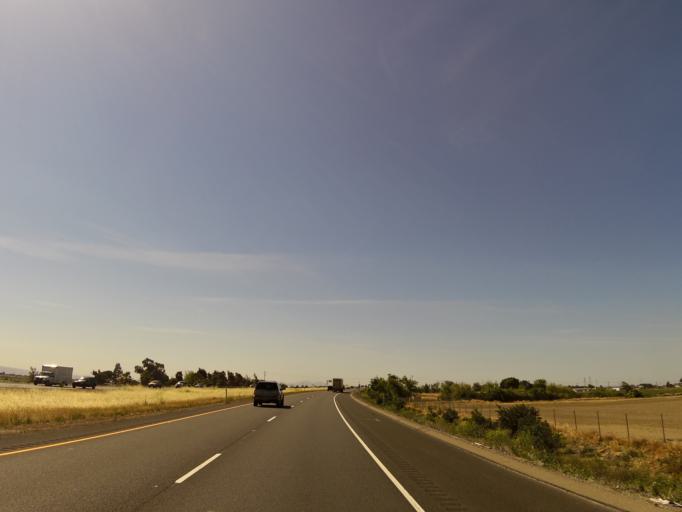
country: US
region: California
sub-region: San Joaquin County
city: Lathrop
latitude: 37.7837
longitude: -121.2645
